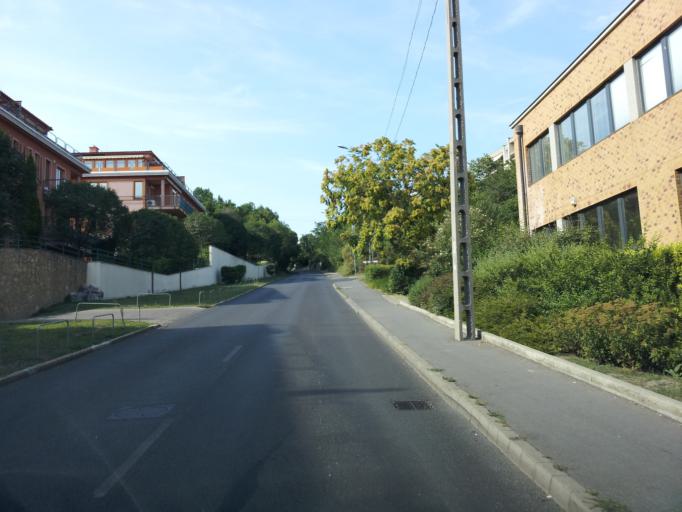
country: HU
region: Budapest
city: Budapest II. keruelet
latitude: 47.5299
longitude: 19.0298
